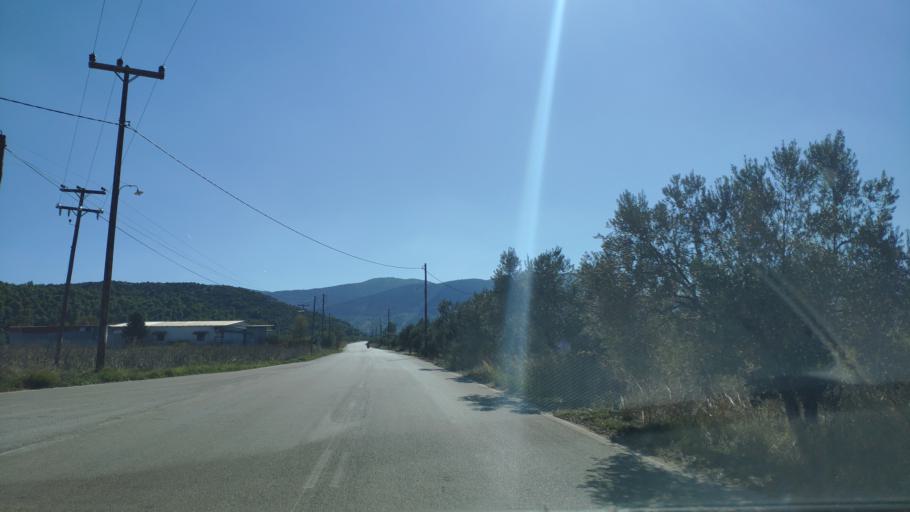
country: GR
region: Peloponnese
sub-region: Nomos Korinthias
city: Athikia
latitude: 37.8363
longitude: 22.9132
